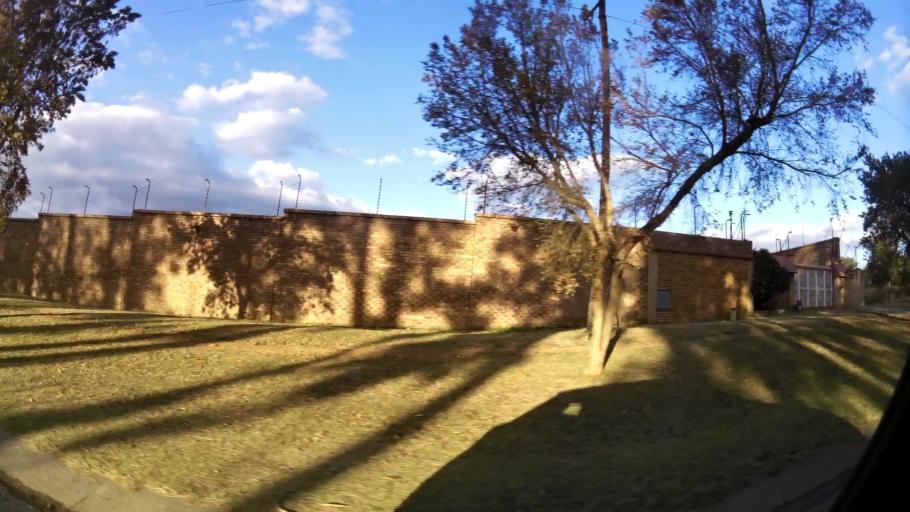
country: ZA
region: Gauteng
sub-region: City of Johannesburg Metropolitan Municipality
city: Midrand
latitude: -25.9521
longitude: 28.1542
